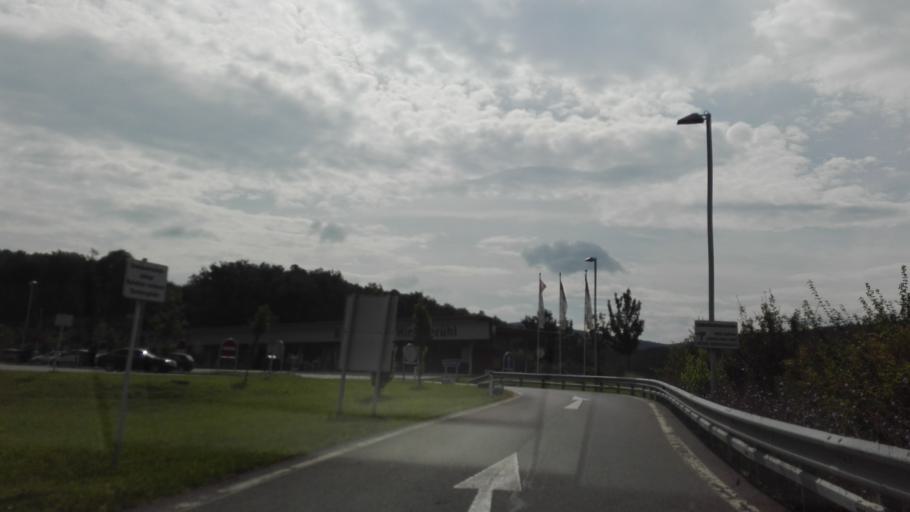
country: AT
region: Lower Austria
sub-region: Politischer Bezirk Modling
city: Gaaden
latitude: 48.0717
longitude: 16.2009
